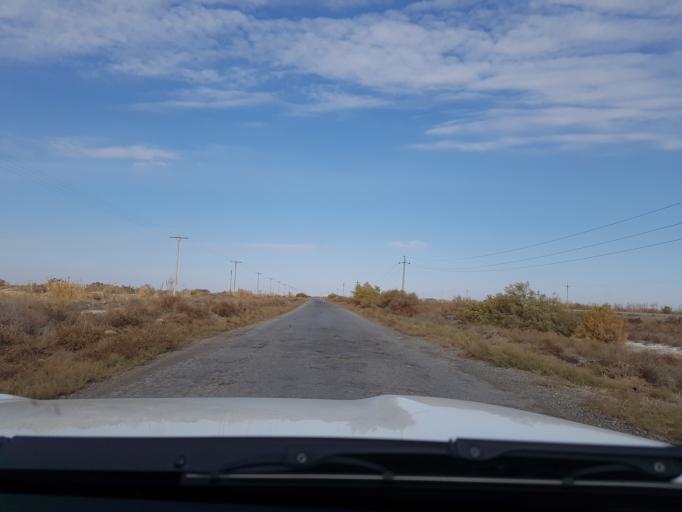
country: TM
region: Ahal
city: Tejen
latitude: 37.4075
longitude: 61.0962
